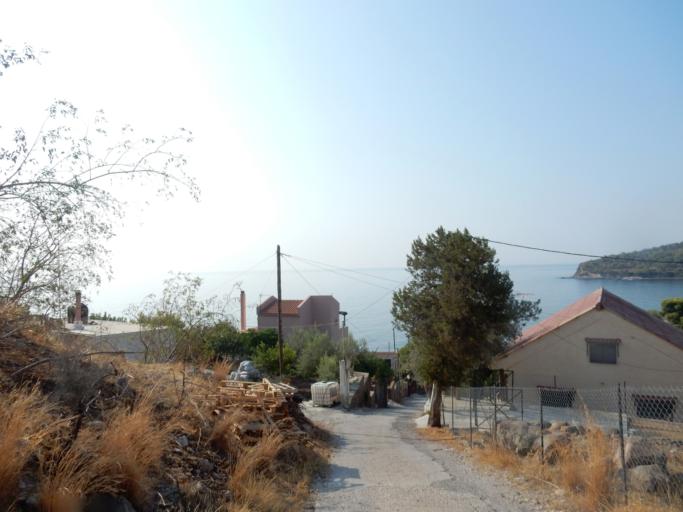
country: GR
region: Attica
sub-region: Nomos Piraios
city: Vathi
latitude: 37.7151
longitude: 23.5228
